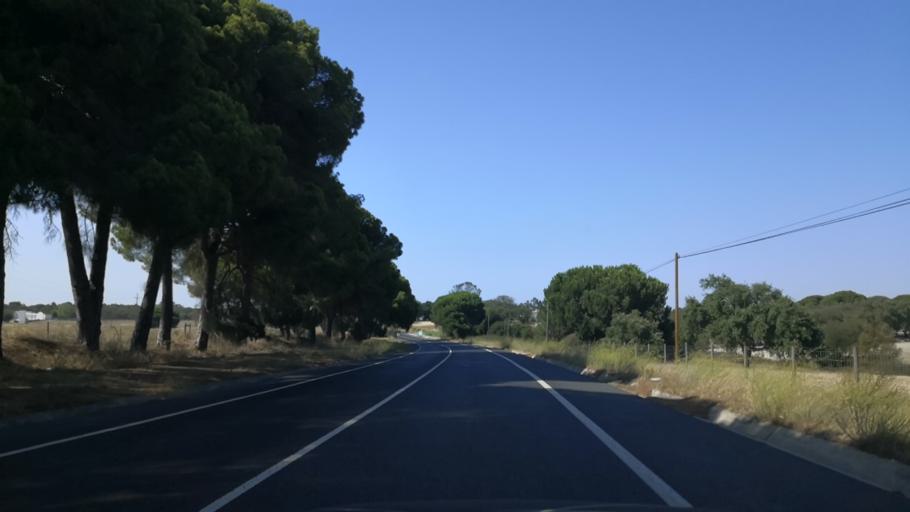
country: PT
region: Evora
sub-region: Vendas Novas
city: Vendas Novas
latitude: 38.6985
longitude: -8.6114
